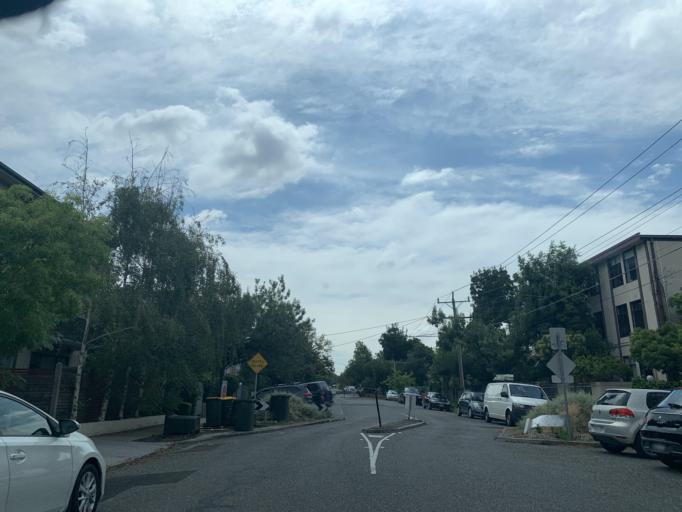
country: AU
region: Victoria
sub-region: Port Phillip
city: Elwood
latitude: -37.8809
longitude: 144.9893
